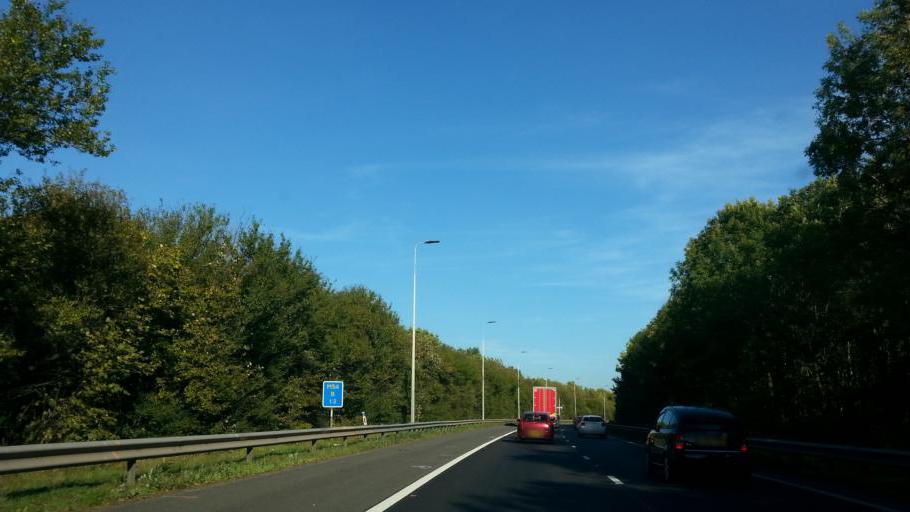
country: GB
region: England
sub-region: Staffordshire
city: Essington
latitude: 52.6375
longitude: -2.0611
